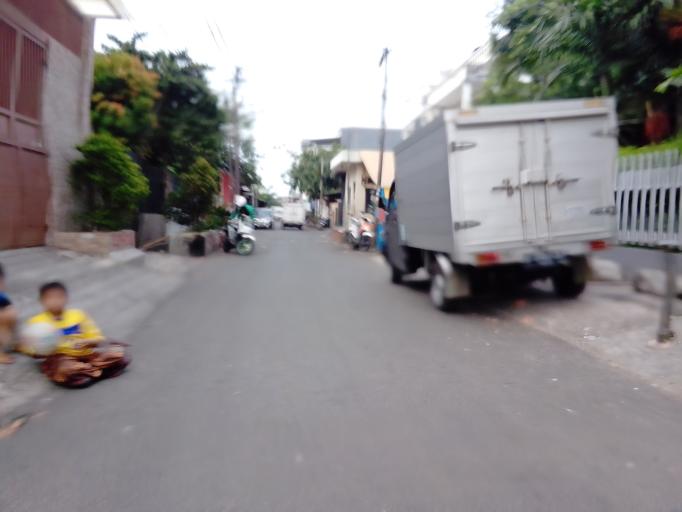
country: ID
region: Jakarta Raya
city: Jakarta
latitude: -6.1558
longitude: 106.8128
